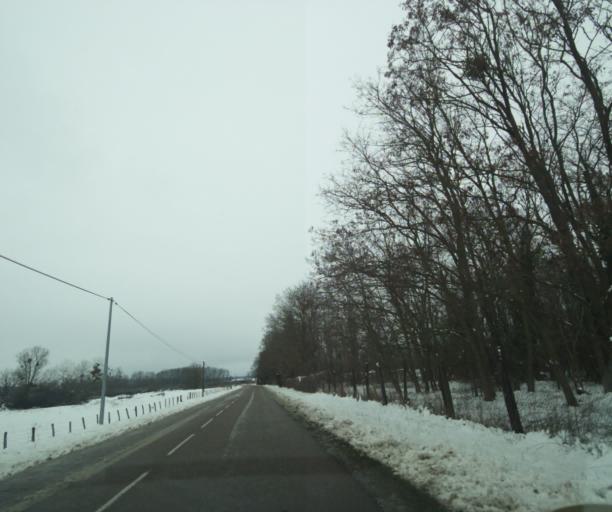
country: FR
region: Champagne-Ardenne
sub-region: Departement de la Haute-Marne
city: Montier-en-Der
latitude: 48.4514
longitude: 4.7776
